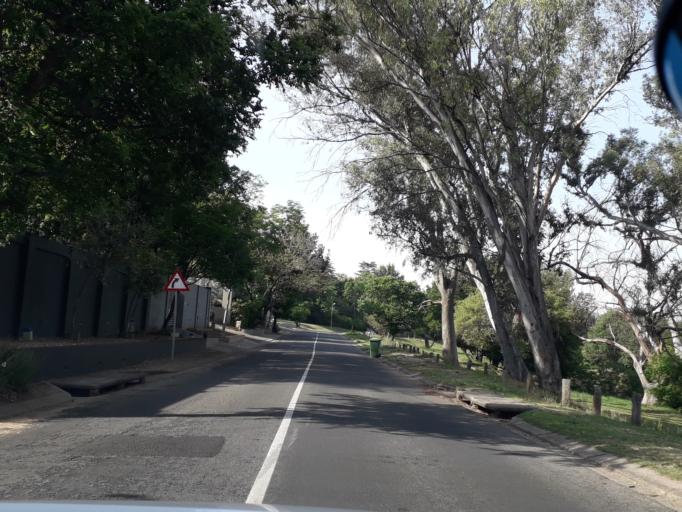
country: ZA
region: Gauteng
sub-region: City of Johannesburg Metropolitan Municipality
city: Midrand
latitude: -26.0636
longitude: 28.0417
